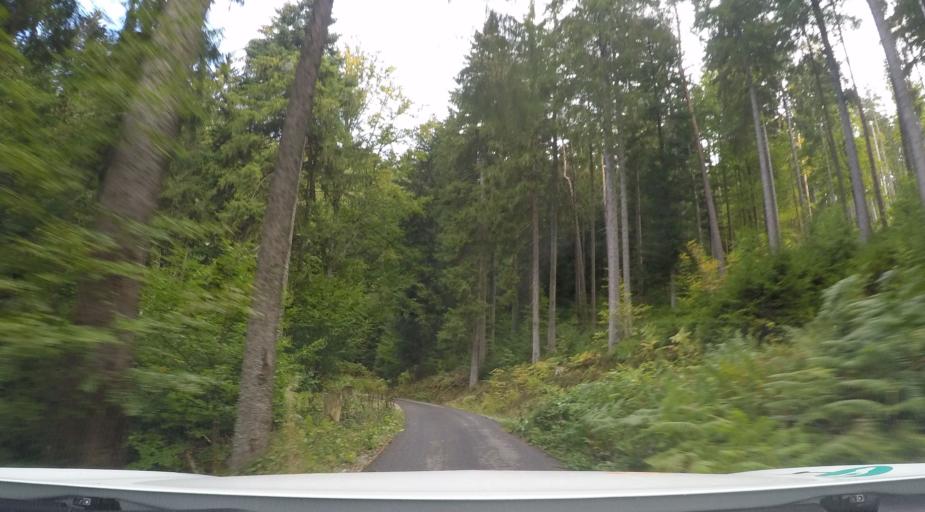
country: DE
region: Baden-Wuerttemberg
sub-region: Karlsruhe Region
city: Baiersbronn
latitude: 48.5496
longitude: 8.3485
